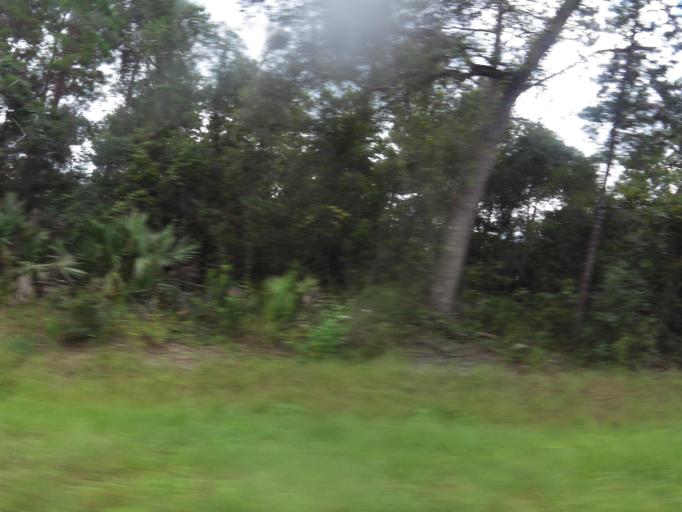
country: US
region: Florida
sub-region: Saint Johns County
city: Palm Valley
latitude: 30.0450
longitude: -81.4067
